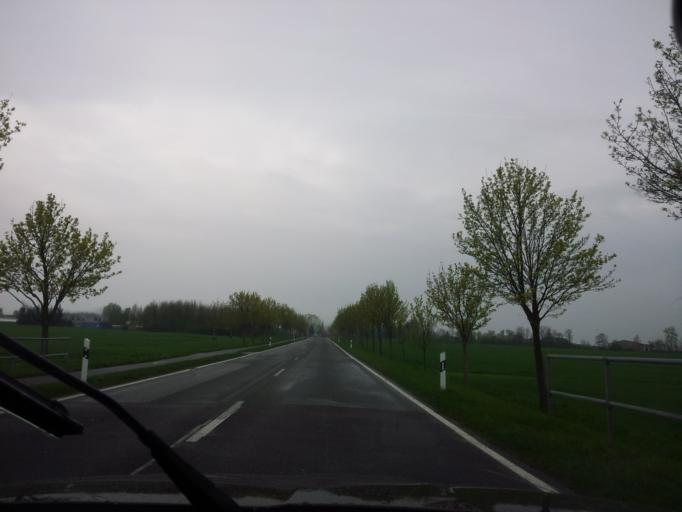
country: DE
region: Saxony-Anhalt
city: Kropstadt
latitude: 52.0073
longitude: 12.7841
